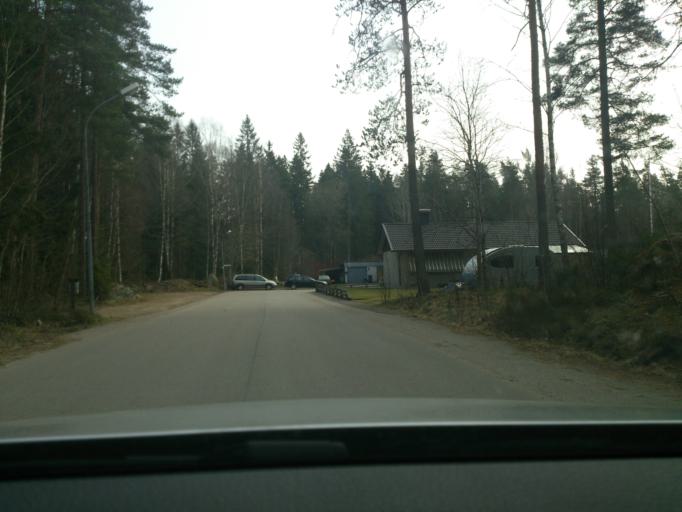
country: SE
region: Kronoberg
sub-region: Alvesta Kommun
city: Moheda
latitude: 57.0011
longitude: 14.5829
